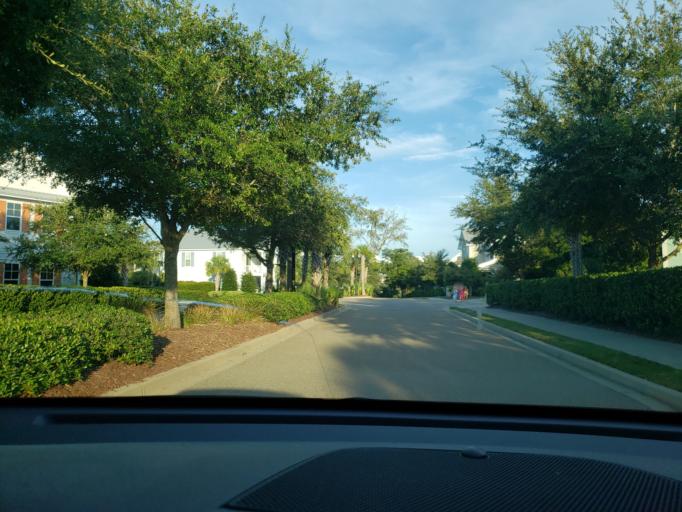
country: US
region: South Carolina
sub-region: Horry County
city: North Myrtle Beach
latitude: 33.7934
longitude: -78.7386
